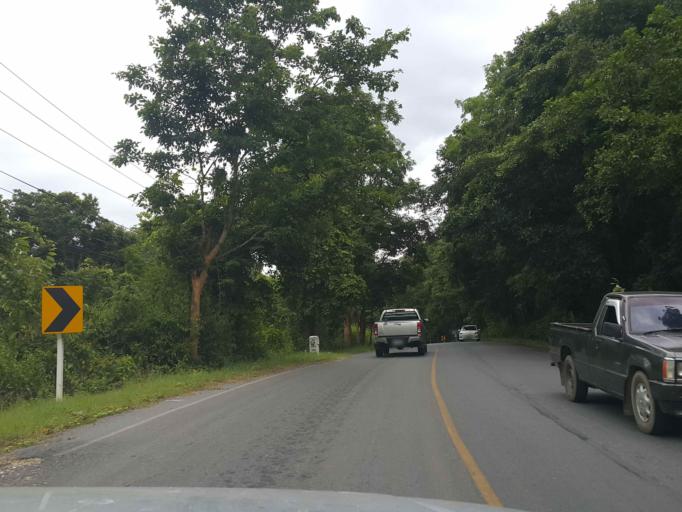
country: TH
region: Lampang
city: Thoen
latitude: 17.6146
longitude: 99.3211
